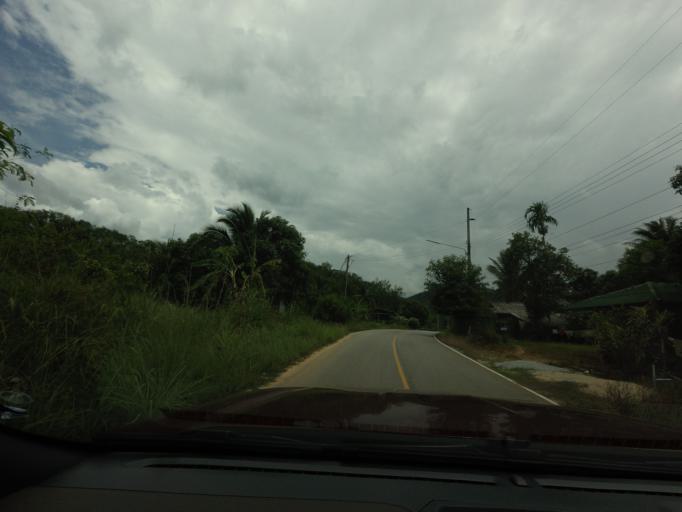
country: TH
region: Narathiwat
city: Chanae
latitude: 6.0364
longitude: 101.6922
